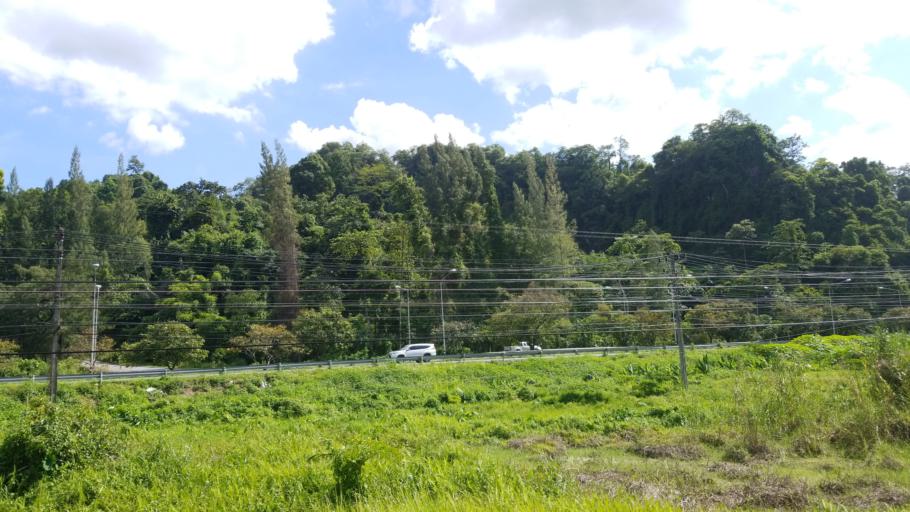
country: TH
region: Nakhon Si Thammarat
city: Thung Song
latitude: 8.1623
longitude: 99.7140
